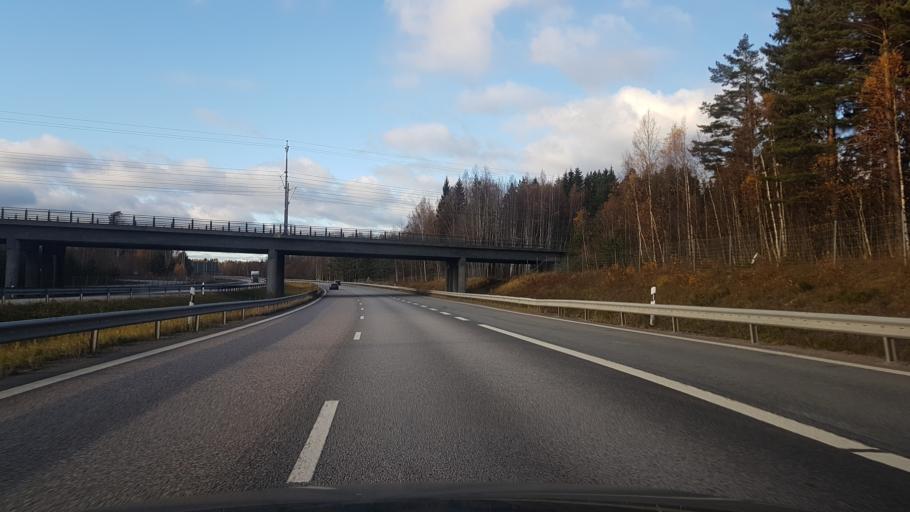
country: SE
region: Uppsala
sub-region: Alvkarleby Kommun
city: AElvkarleby
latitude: 60.4665
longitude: 17.4090
